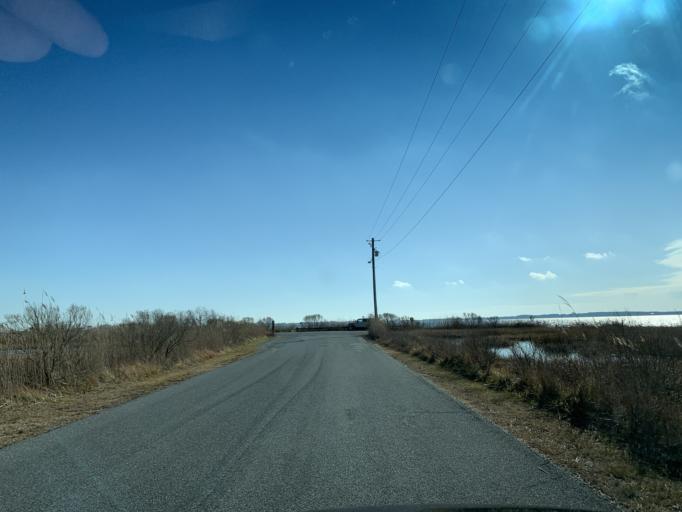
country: US
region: Maryland
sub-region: Worcester County
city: Ocean Pines
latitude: 38.3896
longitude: -75.1088
